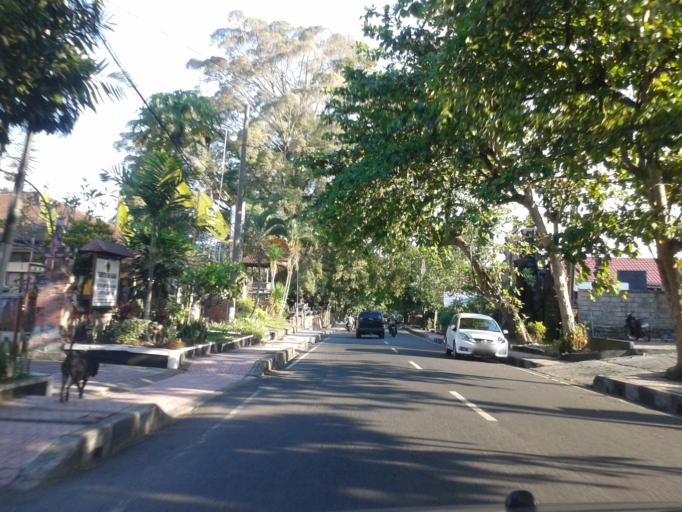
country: ID
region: Bali
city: Klungkung
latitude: -8.5261
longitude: 115.4037
